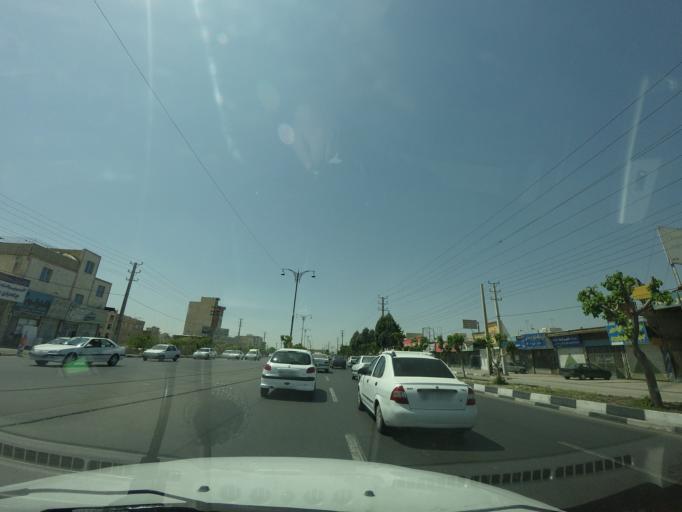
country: IR
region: Tehran
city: Eslamshahr
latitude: 35.5439
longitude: 51.2173
